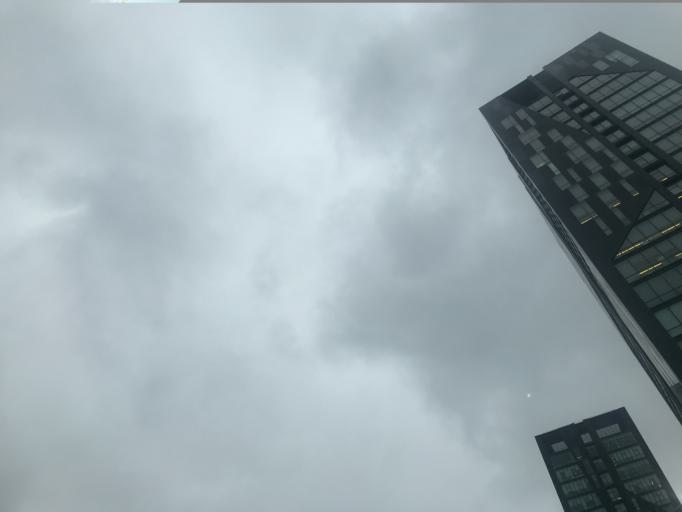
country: TR
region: Istanbul
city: Umraniye
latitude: 41.0261
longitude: 29.1264
